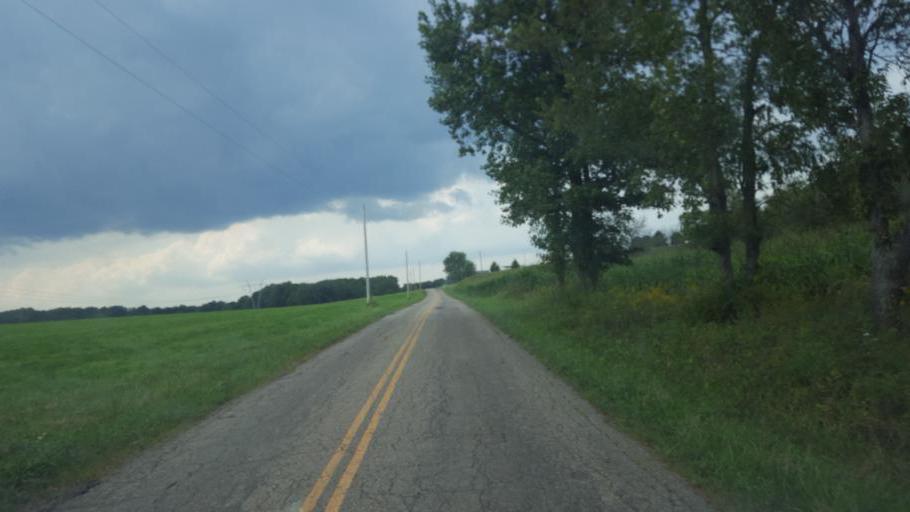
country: US
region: Ohio
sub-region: Knox County
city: Gambier
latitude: 40.3673
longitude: -82.3274
